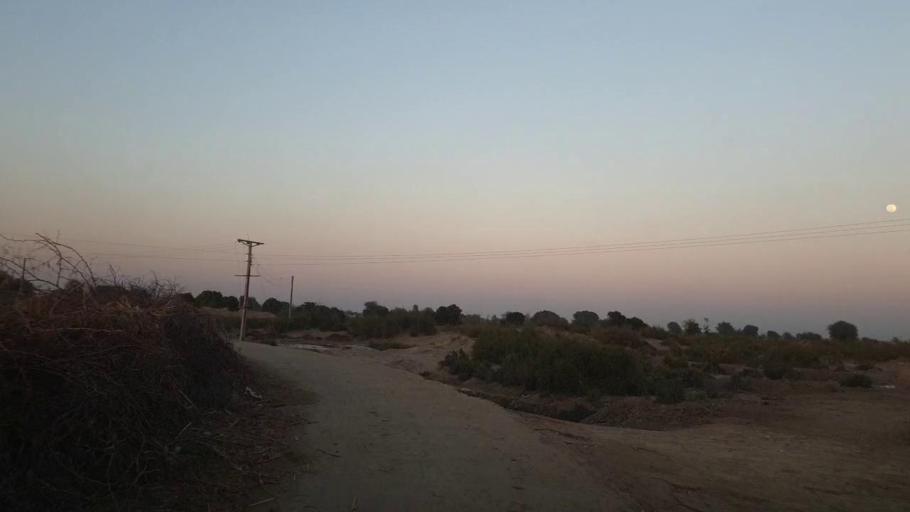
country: PK
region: Sindh
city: Mirpur Khas
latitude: 25.6879
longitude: 69.0536
